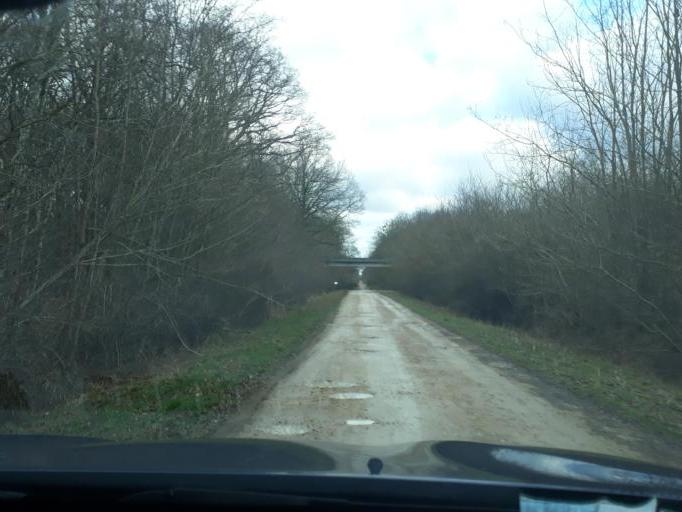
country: FR
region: Centre
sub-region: Departement du Loiret
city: Chevilly
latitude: 48.0124
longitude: 1.8820
